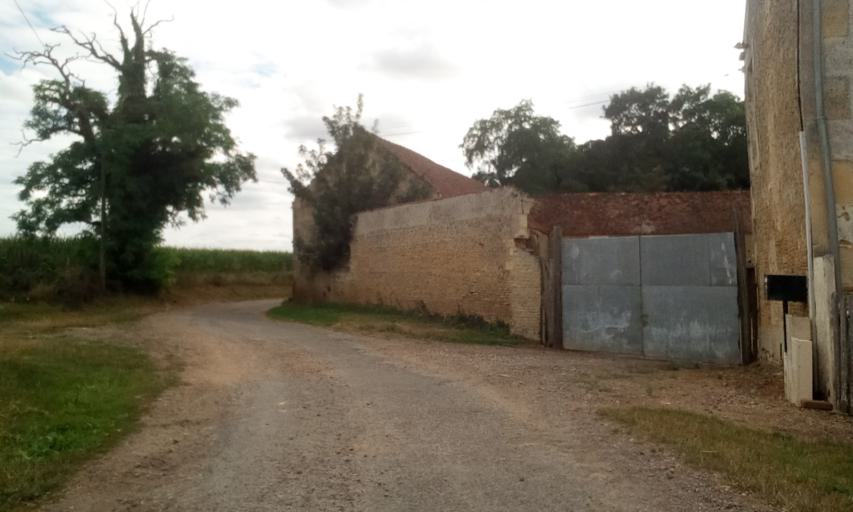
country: FR
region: Lower Normandy
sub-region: Departement du Calvados
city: Bellengreville
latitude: 49.1290
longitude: -0.1938
